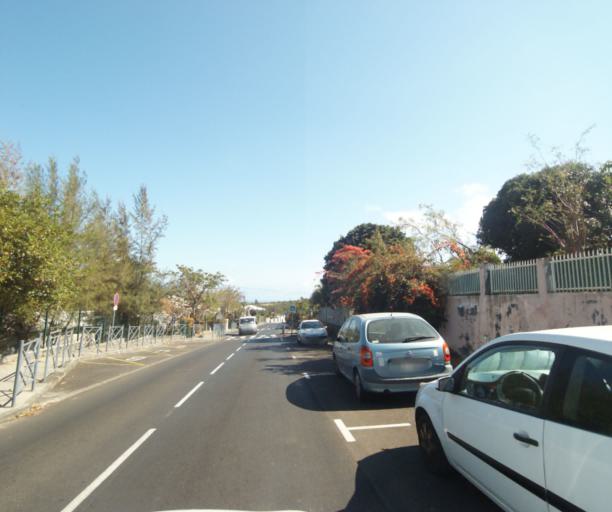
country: RE
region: Reunion
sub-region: Reunion
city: La Possession
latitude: -20.9800
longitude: 55.3241
